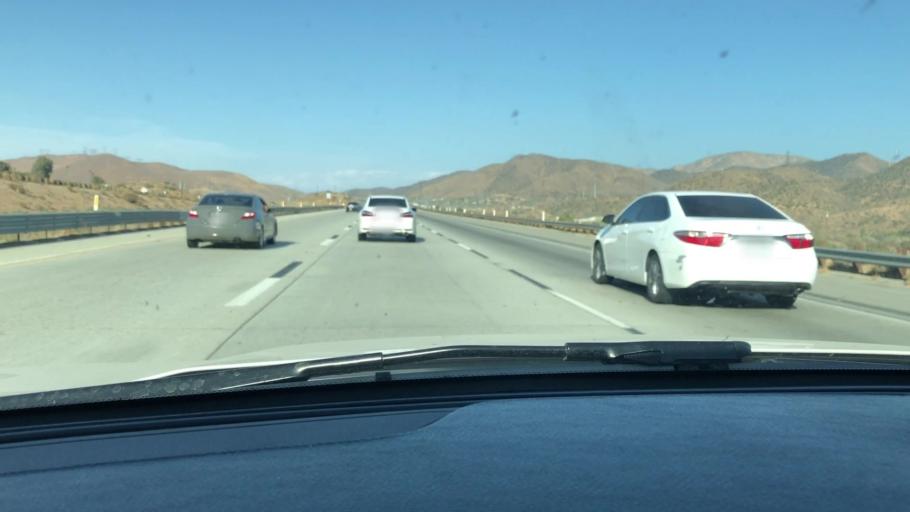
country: US
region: California
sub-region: Los Angeles County
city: Vincent
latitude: 34.4853
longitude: -118.1485
